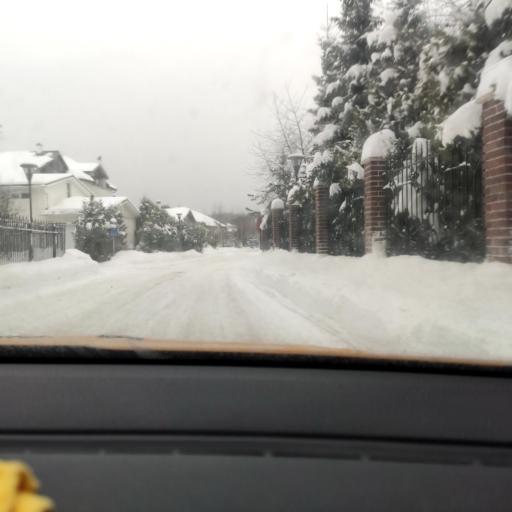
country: RU
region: Moskovskaya
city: Zarech'ye
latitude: 55.6762
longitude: 37.3937
